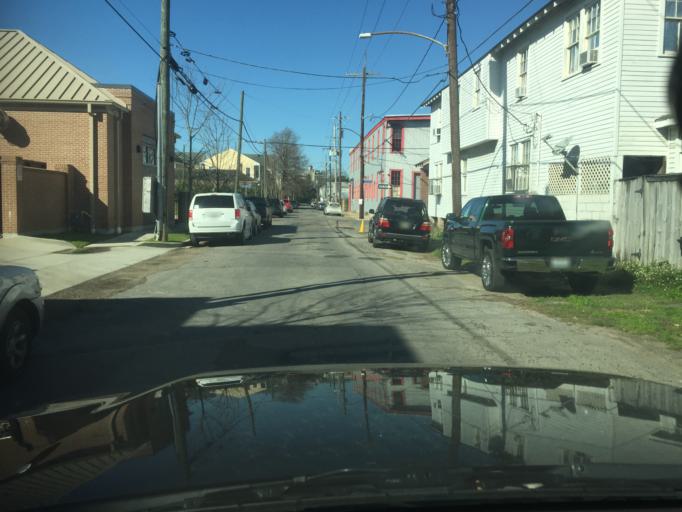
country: US
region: Louisiana
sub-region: Orleans Parish
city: New Orleans
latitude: 29.9331
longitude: -90.0711
